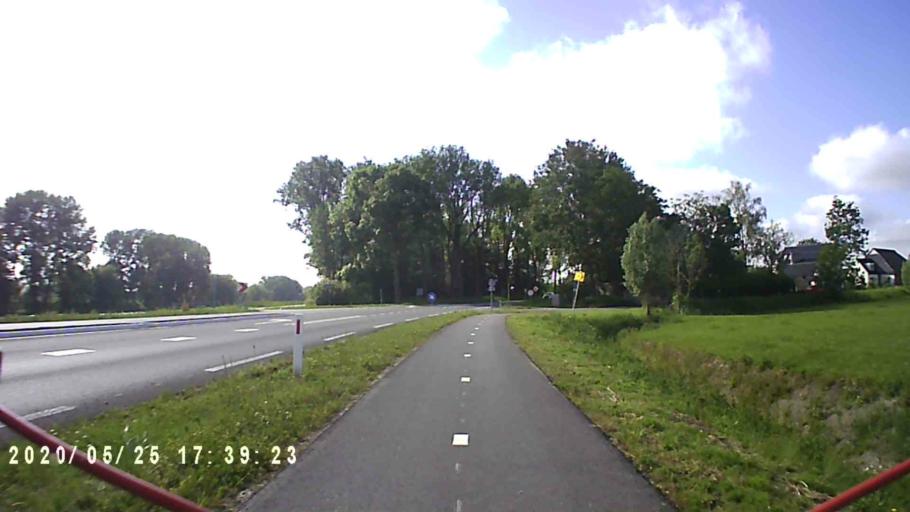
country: NL
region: Groningen
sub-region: Gemeente Groningen
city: Korrewegwijk
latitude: 53.2449
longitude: 6.5509
